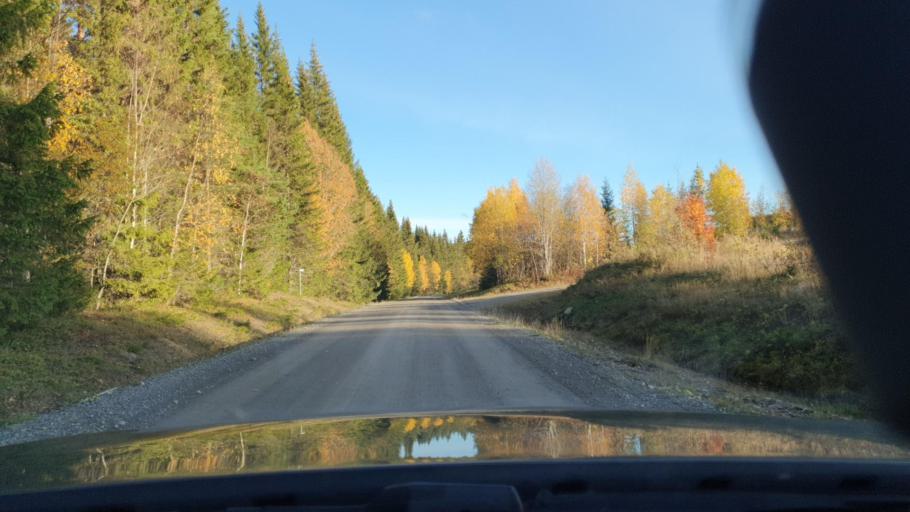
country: SE
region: Jaemtland
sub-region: Stroemsunds Kommun
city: Stroemsund
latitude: 63.5149
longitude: 15.6511
